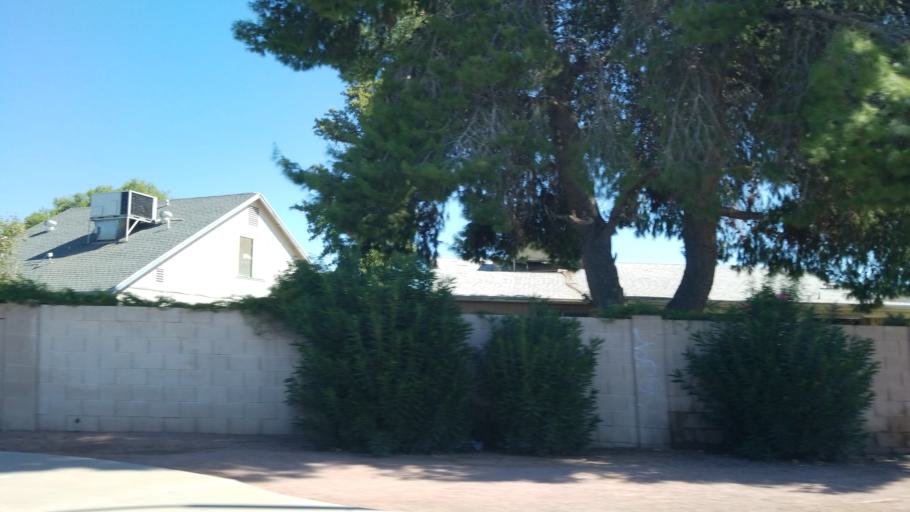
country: US
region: Arizona
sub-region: Maricopa County
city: Tolleson
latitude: 33.4876
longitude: -112.2551
